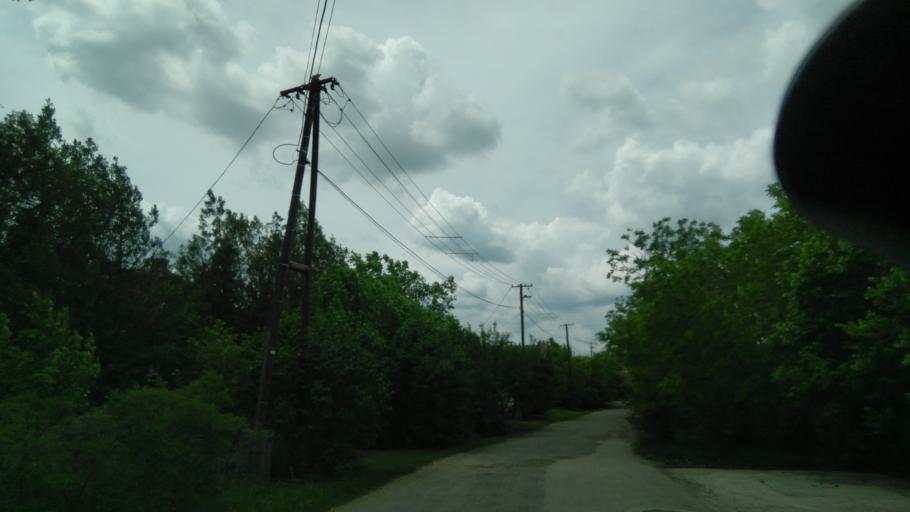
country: HU
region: Bekes
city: Totkomlos
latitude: 46.4148
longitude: 20.7277
